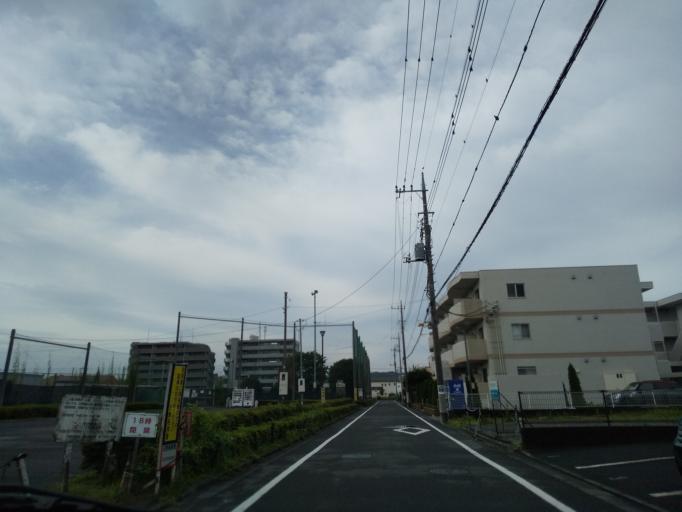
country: JP
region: Tokyo
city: Hino
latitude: 35.6713
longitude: 139.4133
